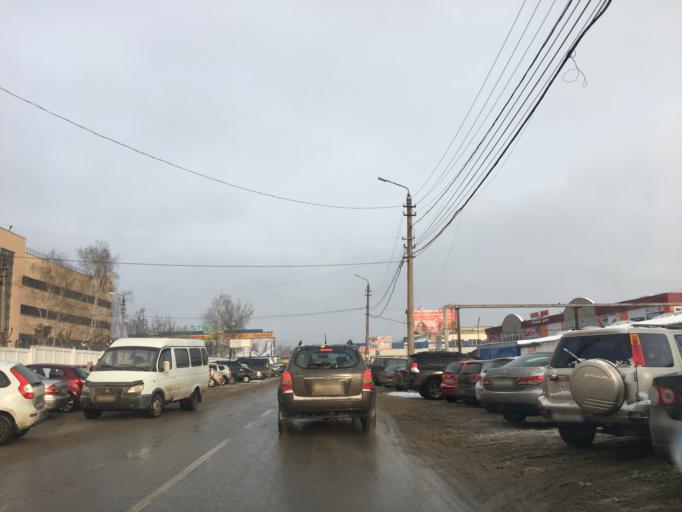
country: RU
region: Tula
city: Tula
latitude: 54.2017
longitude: 37.5918
